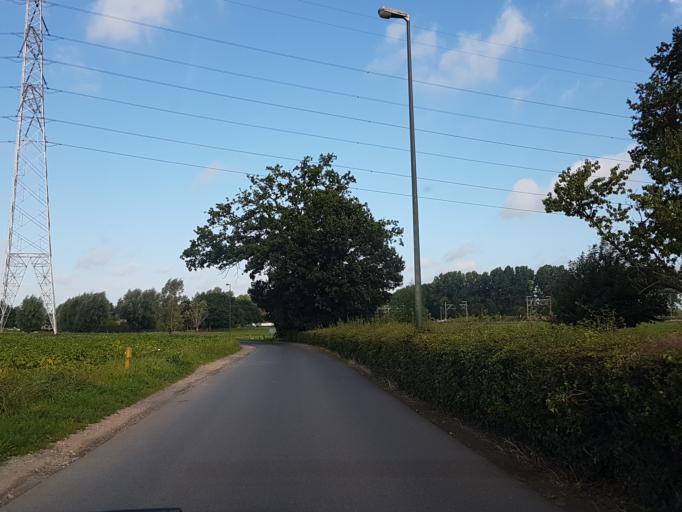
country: BE
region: Flanders
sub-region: Provincie Oost-Vlaanderen
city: Nevele
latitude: 51.0679
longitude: 3.5525
